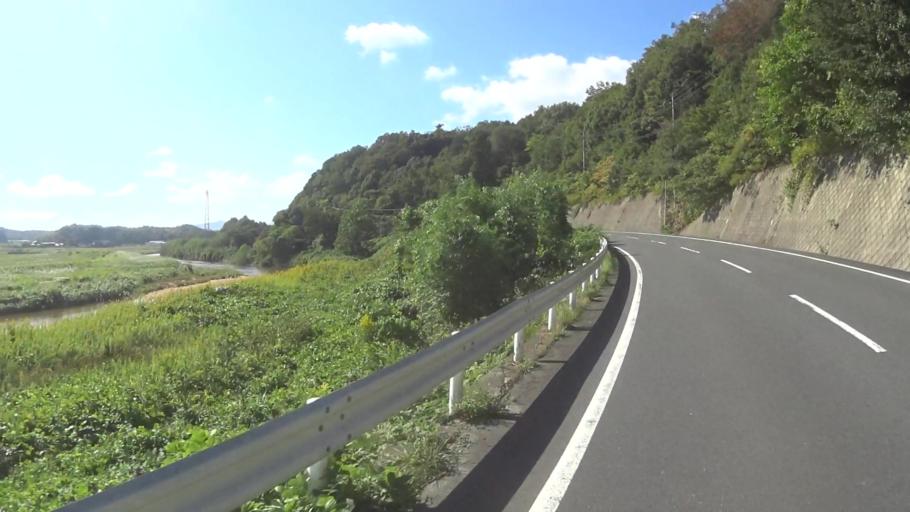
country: JP
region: Kyoto
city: Miyazu
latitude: 35.6496
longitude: 135.0861
